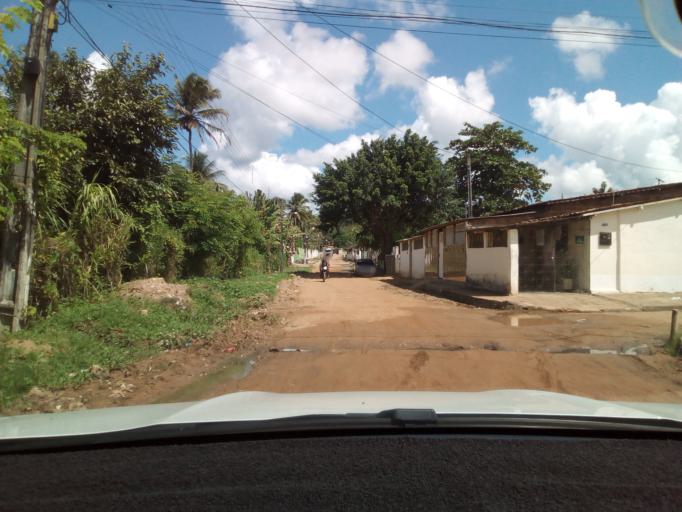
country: BR
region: Paraiba
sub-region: Bayeux
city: Bayeux
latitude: -7.1369
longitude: -34.9324
